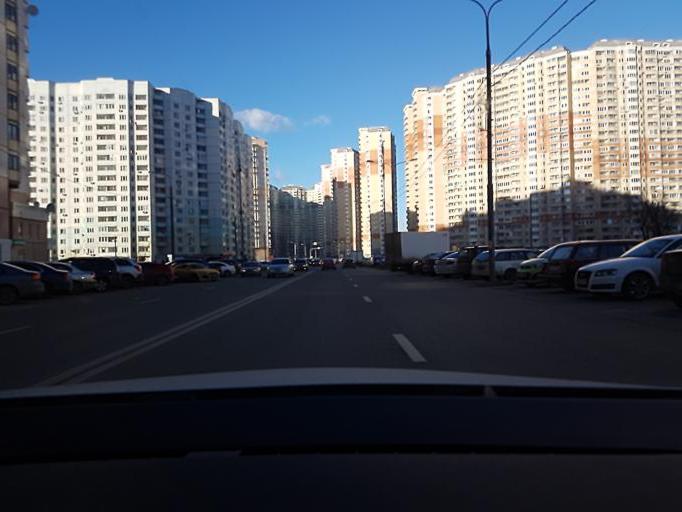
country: RU
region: Moskovskaya
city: Pavshino
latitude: 55.8195
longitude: 37.3745
